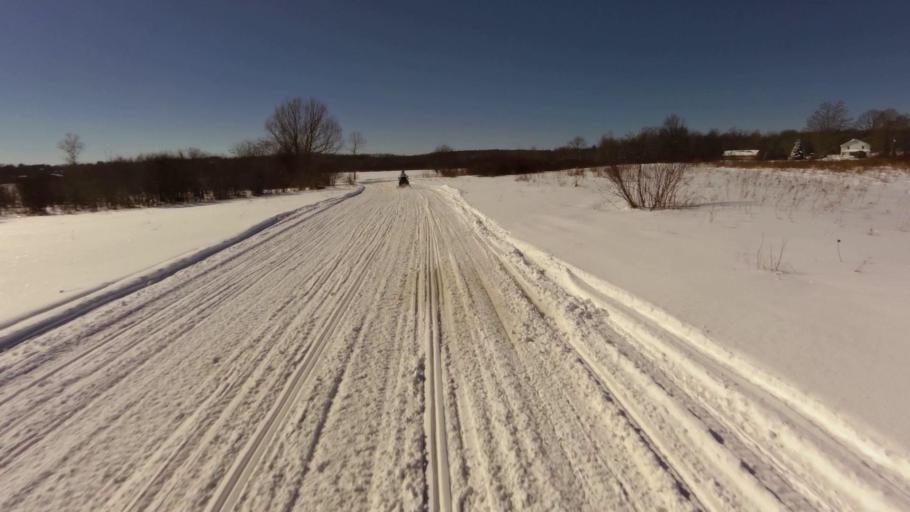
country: US
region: New York
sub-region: Chautauqua County
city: Mayville
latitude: 42.2720
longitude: -79.4865
